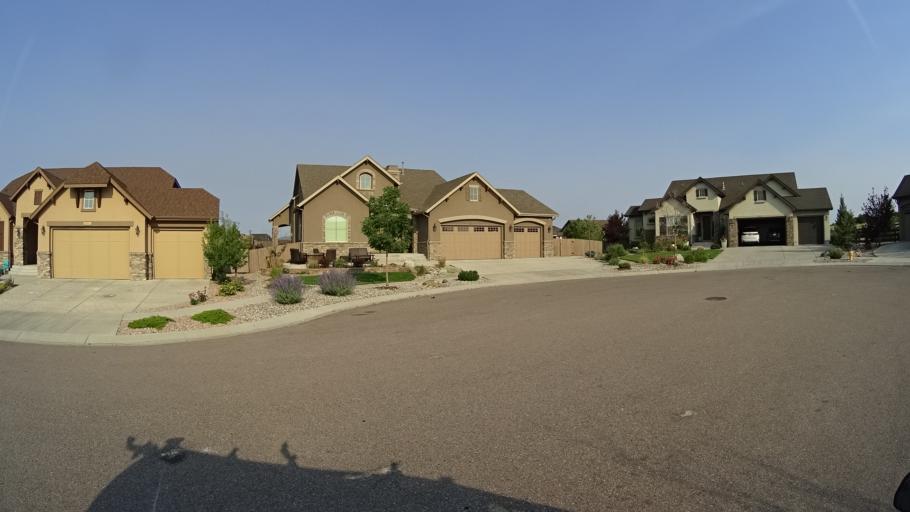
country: US
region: Colorado
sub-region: El Paso County
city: Black Forest
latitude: 38.9755
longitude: -104.7307
